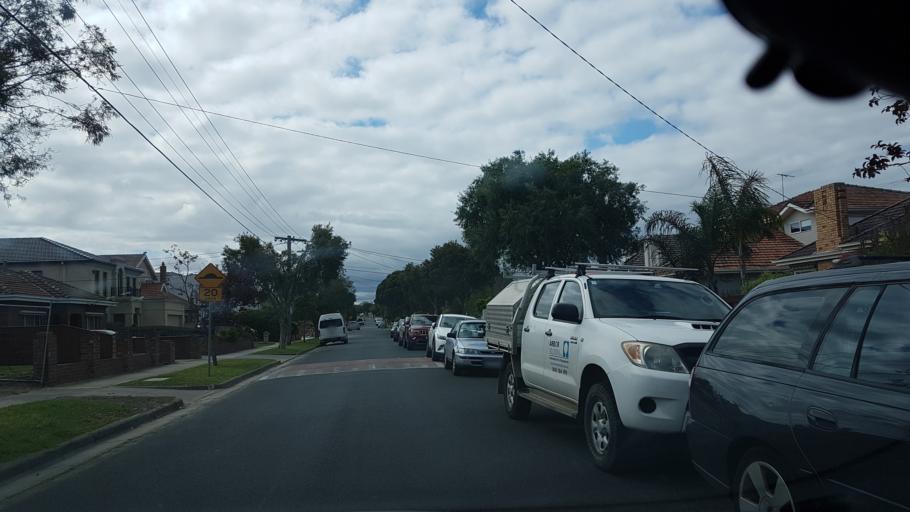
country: AU
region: Victoria
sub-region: Glen Eira
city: Bentleigh
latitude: -37.9250
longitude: 145.0373
